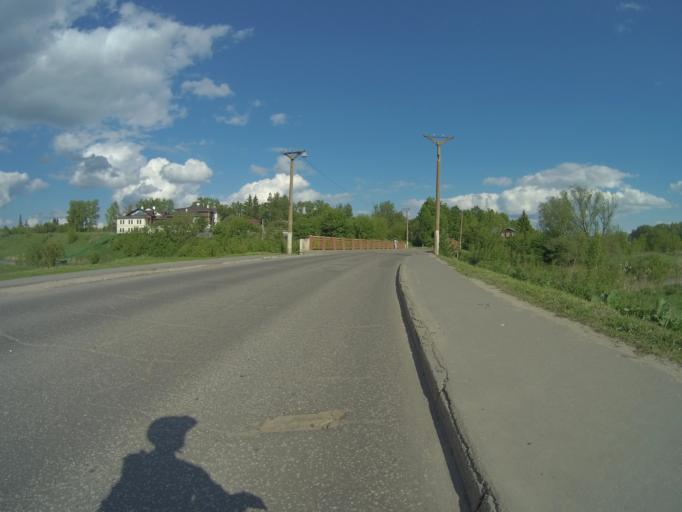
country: RU
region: Vladimir
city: Suzdal'
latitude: 56.4250
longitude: 40.4368
